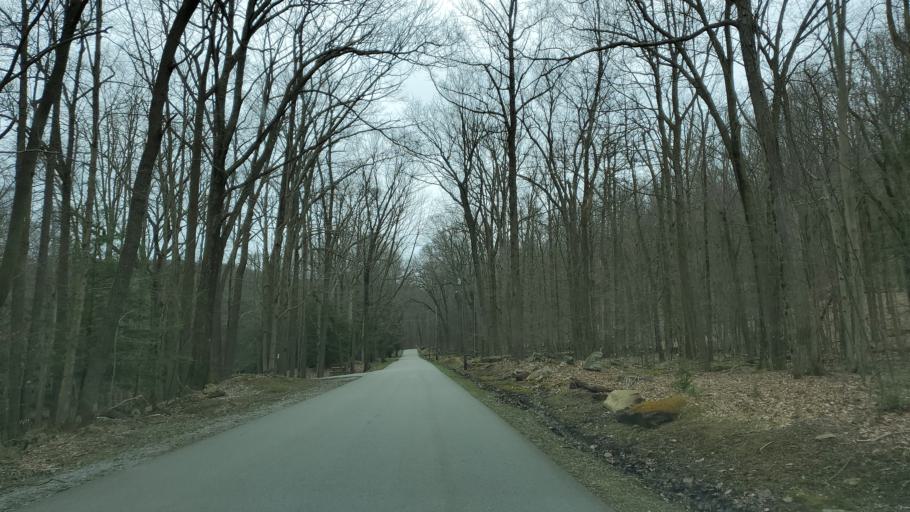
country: US
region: Pennsylvania
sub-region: Westmoreland County
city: Ligonier
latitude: 40.1571
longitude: -79.2299
